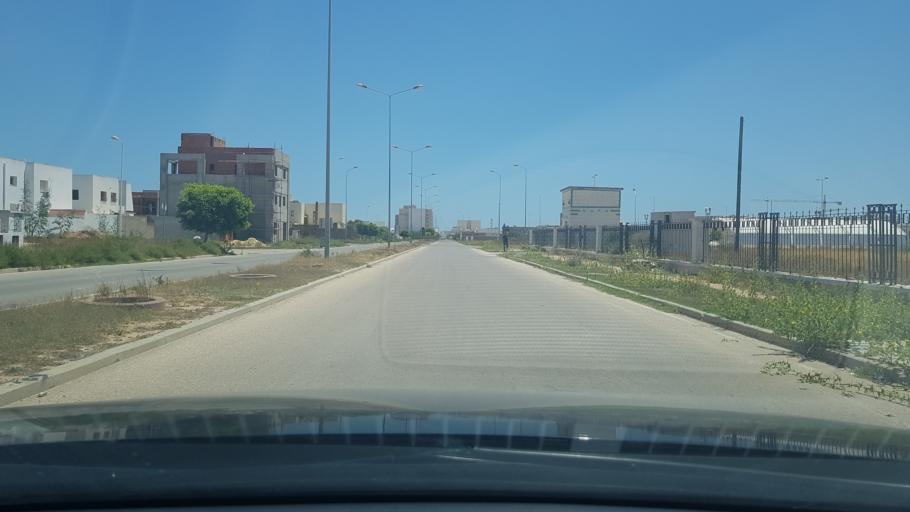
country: TN
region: Safaqis
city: Al Qarmadah
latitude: 34.8391
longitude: 10.7584
